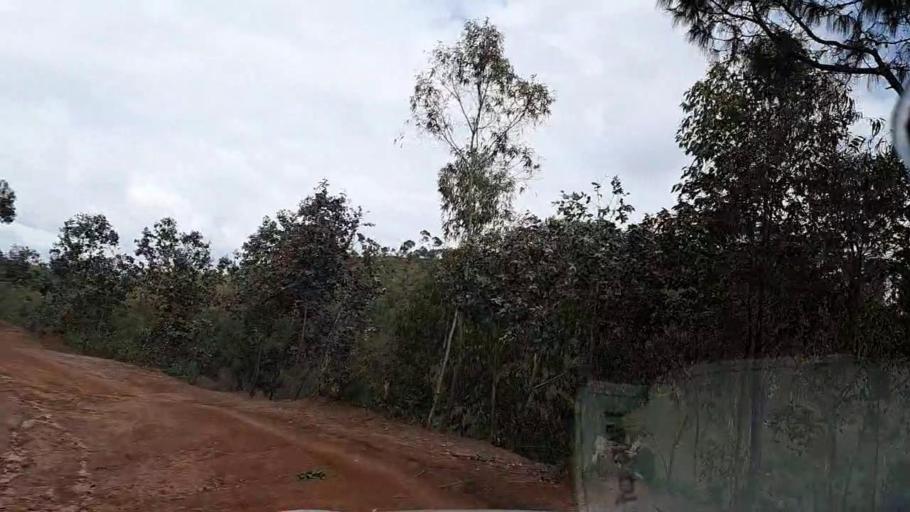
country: RW
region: Southern Province
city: Nzega
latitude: -2.4121
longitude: 29.4546
